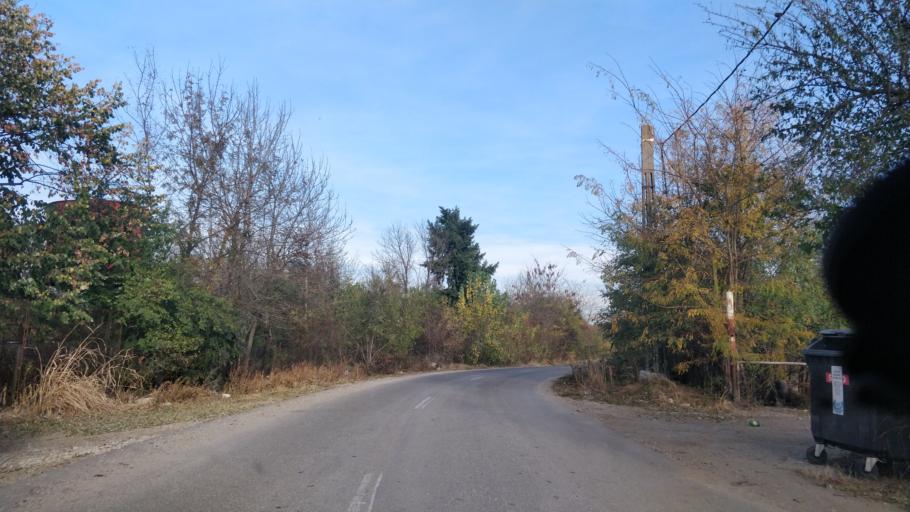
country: RO
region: Giurgiu
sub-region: Comuna Bucsani
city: Bucsani
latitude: 44.3359
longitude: 25.6440
